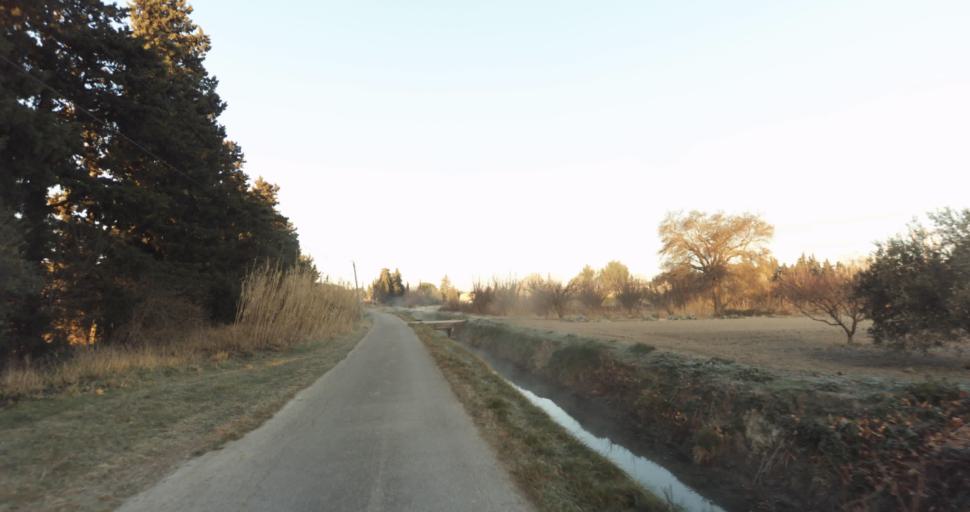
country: FR
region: Provence-Alpes-Cote d'Azur
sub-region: Departement des Bouches-du-Rhone
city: Barbentane
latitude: 43.9004
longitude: 4.7738
